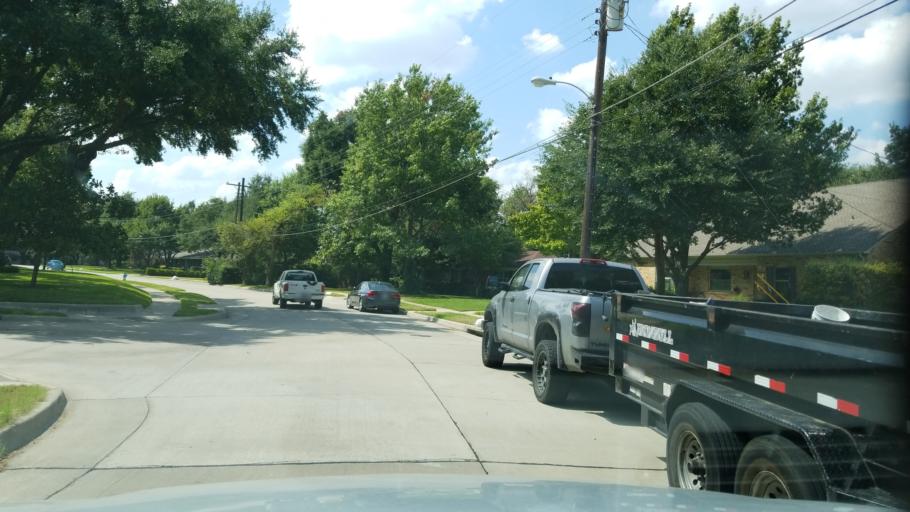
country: US
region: Texas
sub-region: Dallas County
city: Richardson
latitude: 32.9550
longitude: -96.7509
